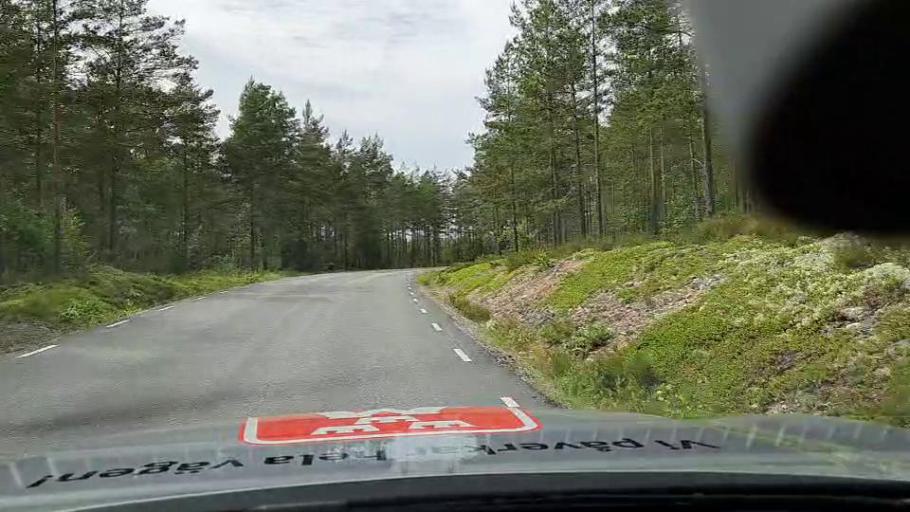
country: SE
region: Soedermanland
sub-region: Eskilstuna Kommun
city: Arla
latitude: 59.2319
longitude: 16.7289
